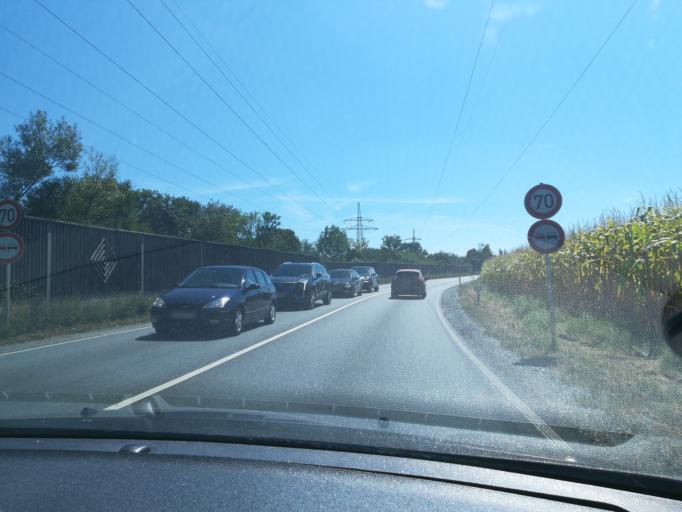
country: DE
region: Bavaria
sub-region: Upper Bavaria
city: Hohenlinden
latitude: 48.1548
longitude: 11.9873
